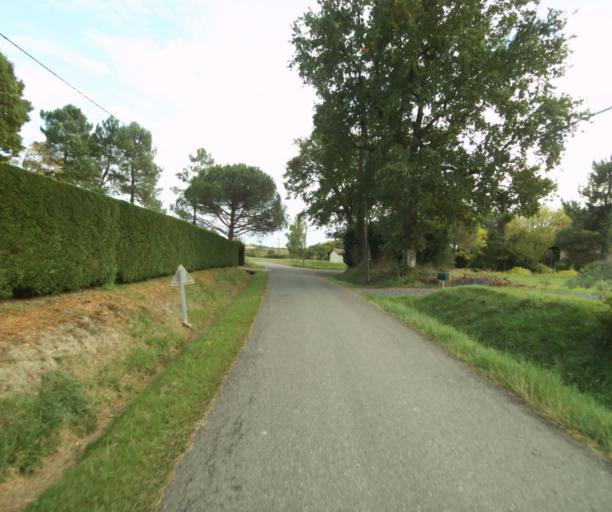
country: FR
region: Midi-Pyrenees
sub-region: Departement du Gers
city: Eauze
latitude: 43.8880
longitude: 0.0704
